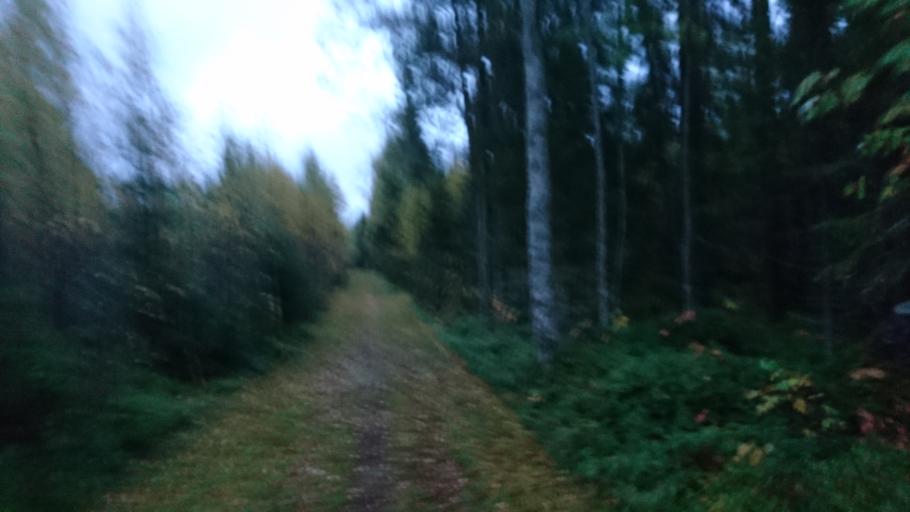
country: SE
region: Vaesterbotten
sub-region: Robertsfors Kommun
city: Robertsfors
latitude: 64.2290
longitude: 20.9993
